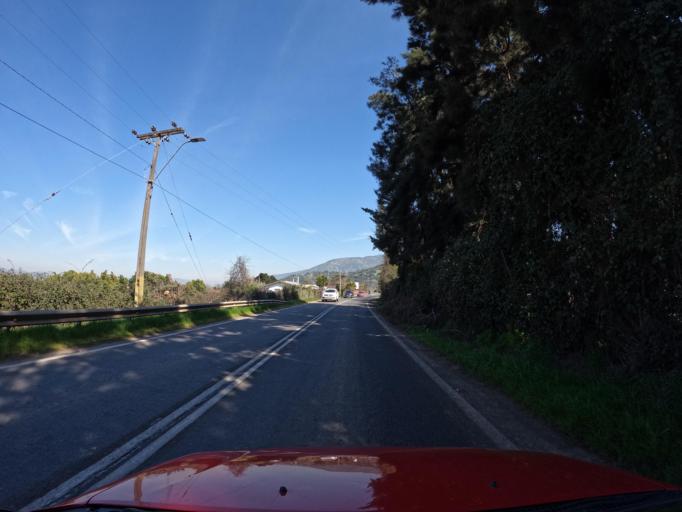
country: CL
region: Maule
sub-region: Provincia de Curico
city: Rauco
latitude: -34.9813
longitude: -71.4111
